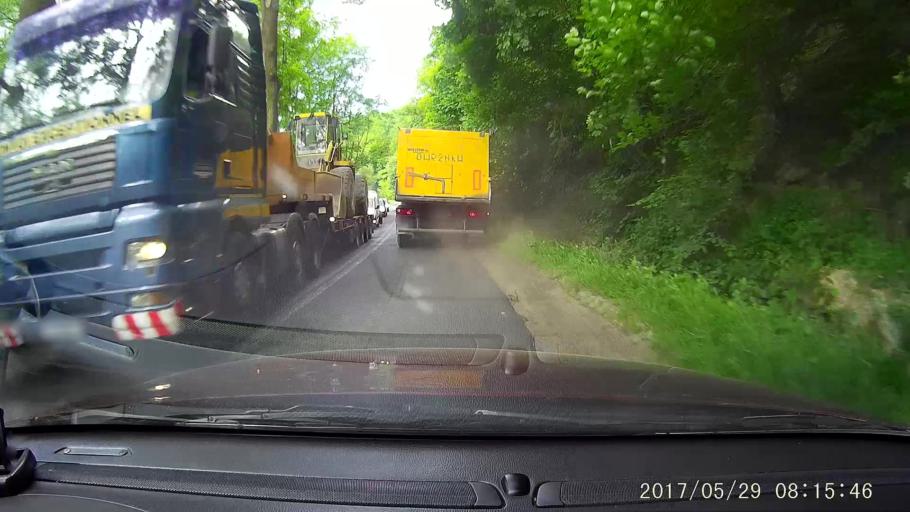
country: PL
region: Lower Silesian Voivodeship
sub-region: Powiat zlotoryjski
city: Zlotoryja
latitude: 51.1228
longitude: 15.8907
